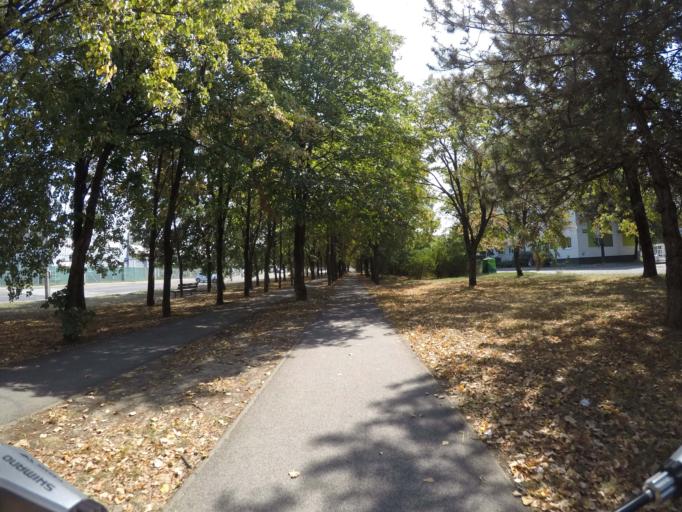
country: SK
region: Bratislavsky
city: Dunajska Luzna
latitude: 48.1439
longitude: 17.2126
